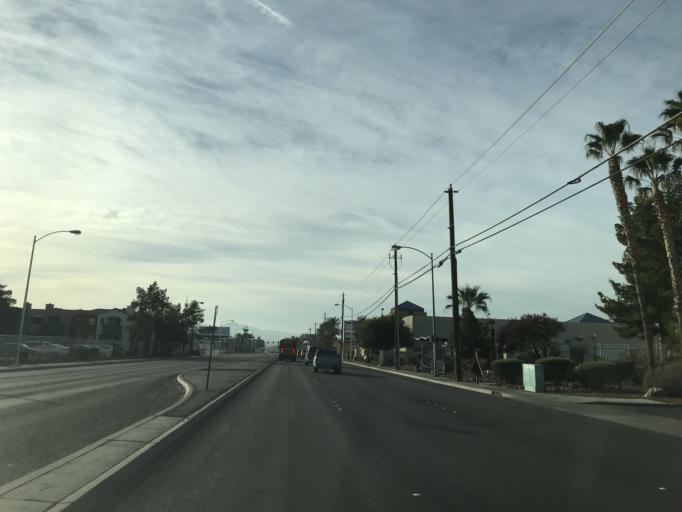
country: US
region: Nevada
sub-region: Clark County
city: Winchester
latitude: 36.1403
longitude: -115.0655
